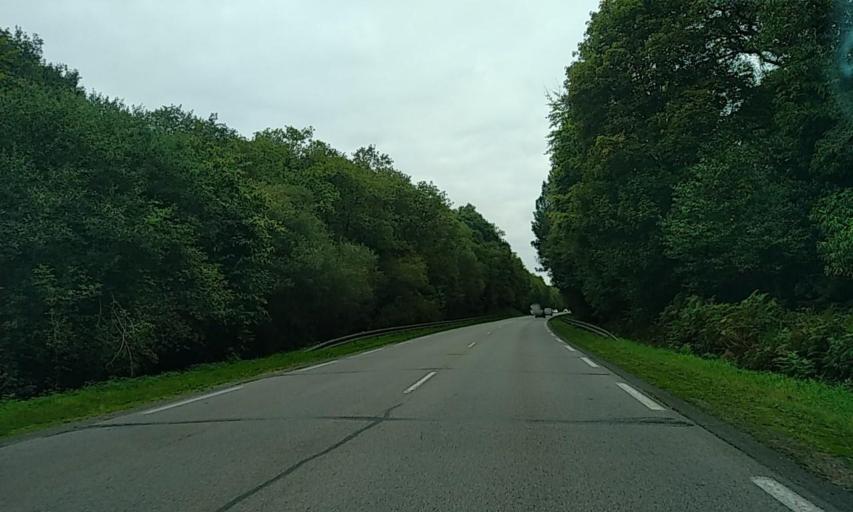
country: FR
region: Brittany
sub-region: Departement du Morbihan
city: Caudan
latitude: 47.8078
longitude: -3.3352
